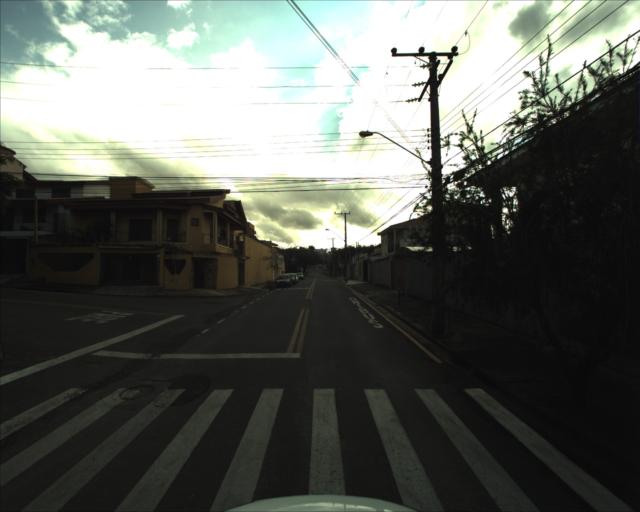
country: BR
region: Sao Paulo
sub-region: Sorocaba
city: Sorocaba
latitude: -23.5245
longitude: -47.4787
